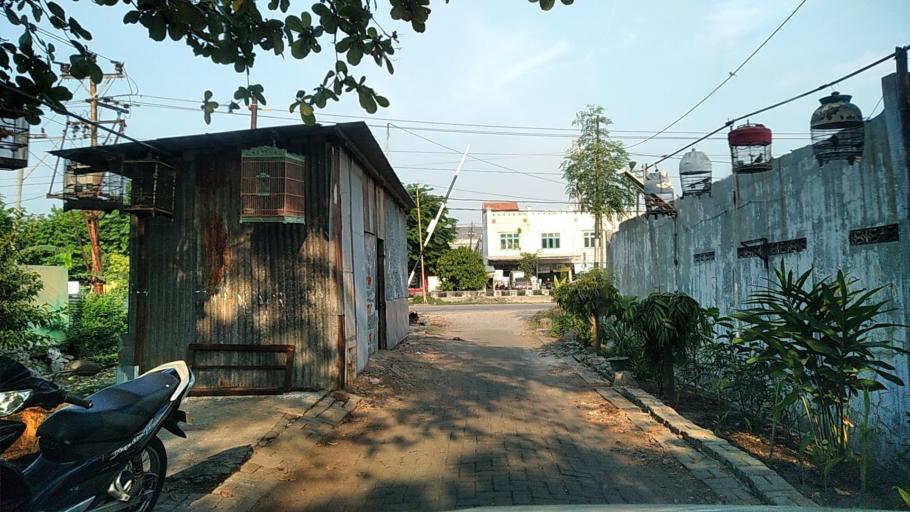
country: ID
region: Central Java
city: Semarang
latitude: -6.9646
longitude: 110.4104
